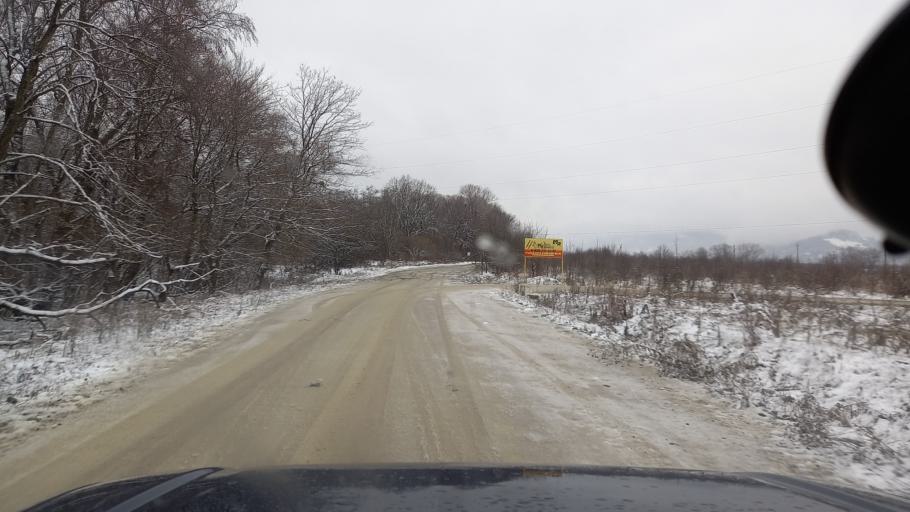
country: RU
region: Adygeya
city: Kamennomostskiy
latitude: 44.2297
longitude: 40.1864
